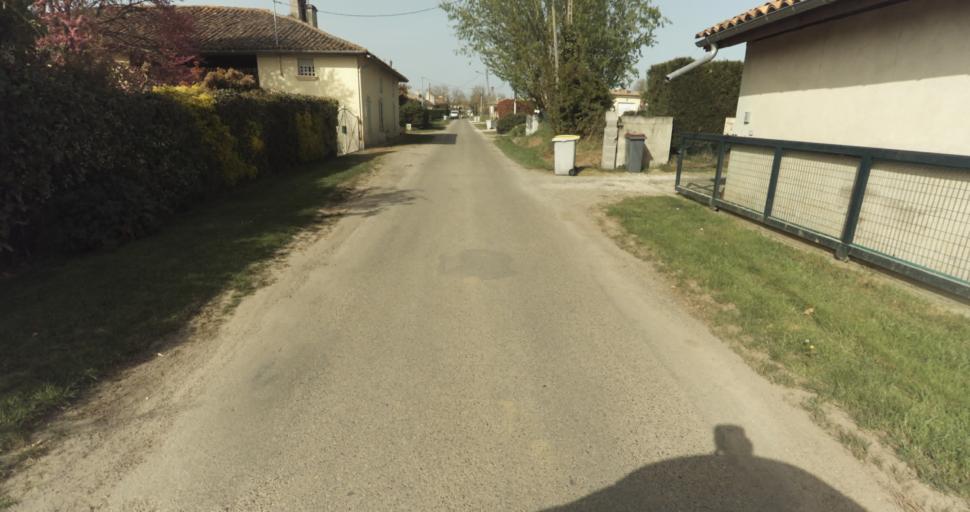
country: FR
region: Midi-Pyrenees
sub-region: Departement du Tarn-et-Garonne
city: Moissac
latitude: 44.1205
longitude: 1.1613
